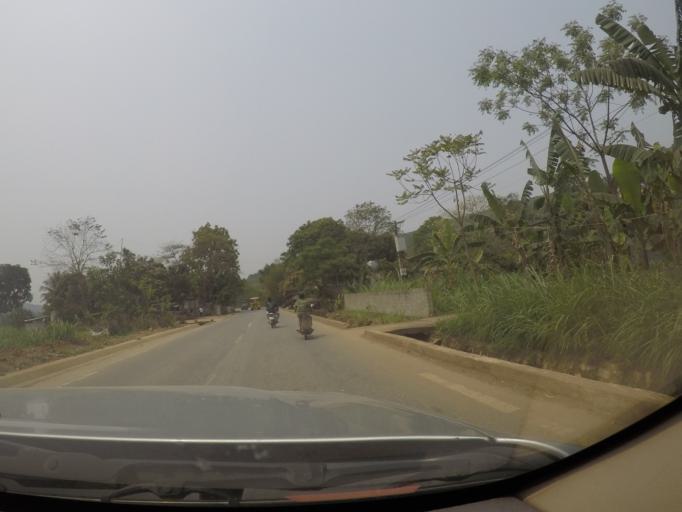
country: VN
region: Thanh Hoa
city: Thi Tran Cam Thuy
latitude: 20.1560
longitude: 105.4569
